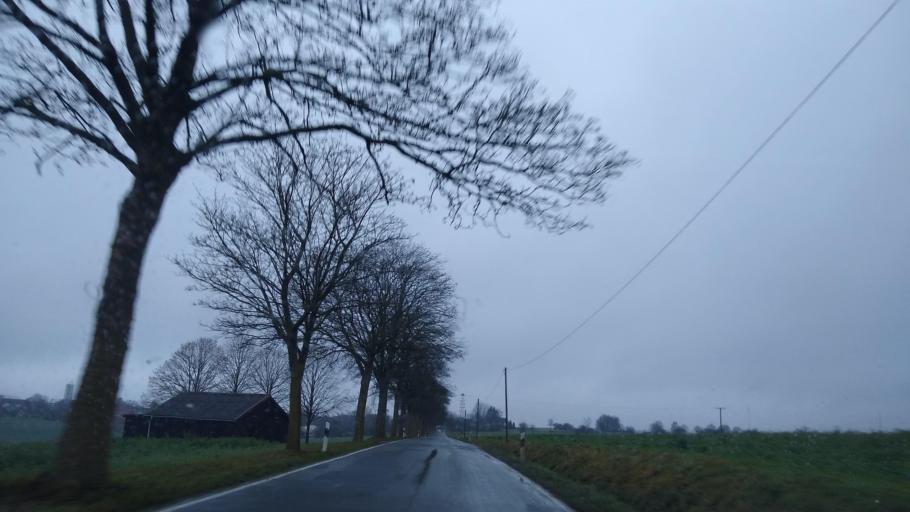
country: DE
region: Lower Saxony
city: Vahlbruch
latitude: 51.9226
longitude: 9.3537
